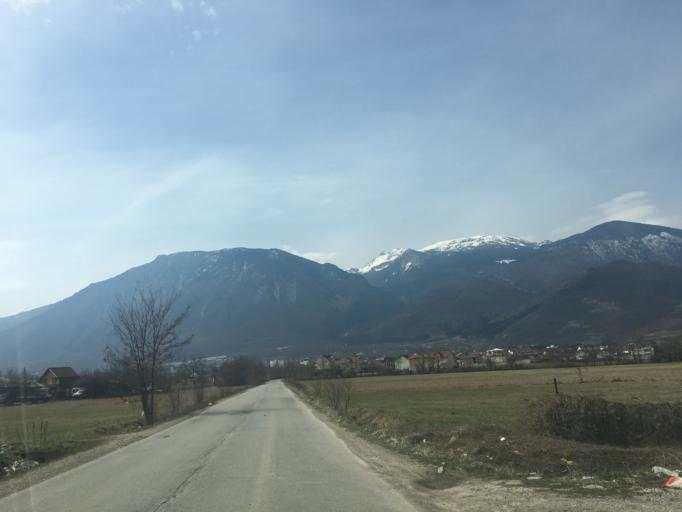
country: XK
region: Pec
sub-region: Komuna e Pejes
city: Peje
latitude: 42.6436
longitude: 20.3108
